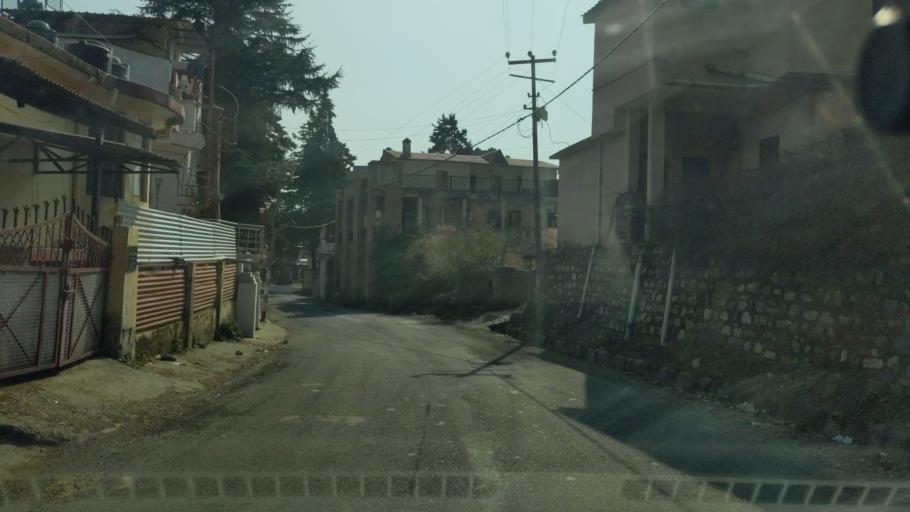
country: IN
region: Uttarakhand
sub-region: Naini Tal
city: Bhowali
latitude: 29.3871
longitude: 79.5289
